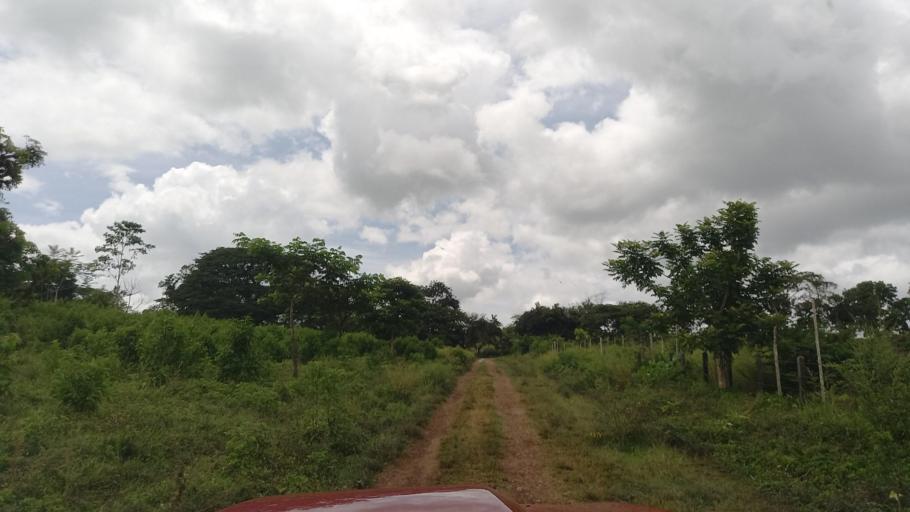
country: NI
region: Nueva Segovia
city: Wiwili
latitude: 13.4483
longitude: -85.7232
